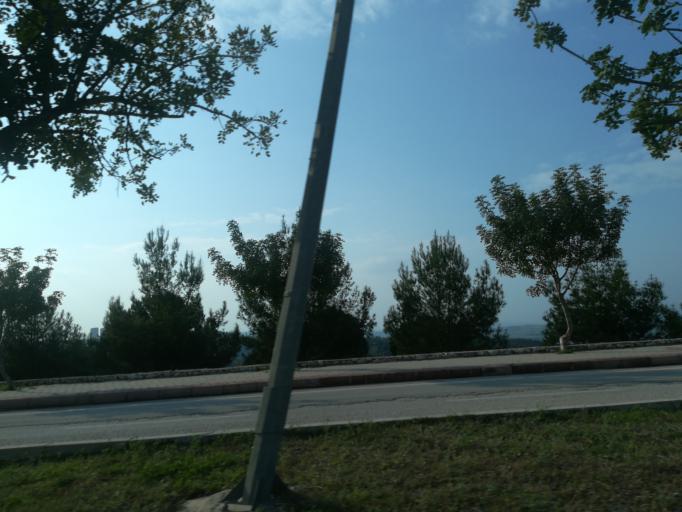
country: TR
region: Adana
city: Adana
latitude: 37.0705
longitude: 35.3796
